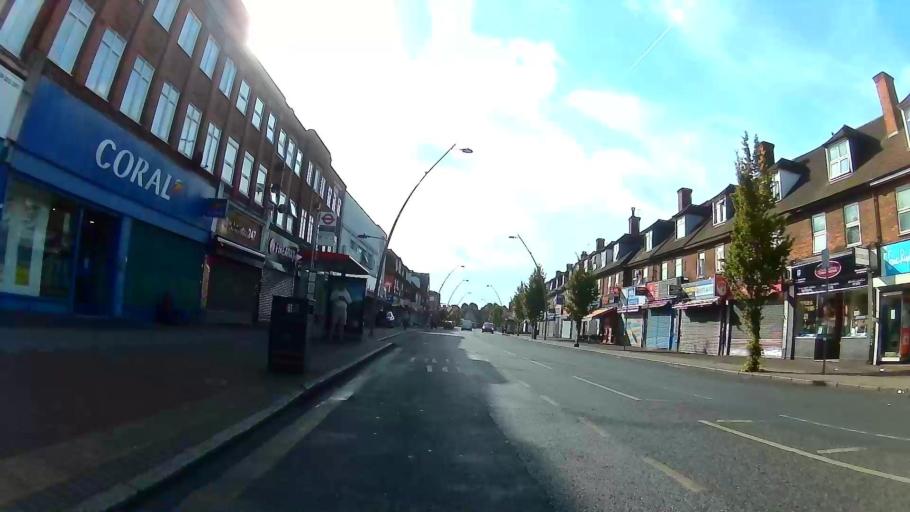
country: GB
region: England
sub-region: Greater London
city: Becontree
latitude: 51.5625
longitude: 0.1222
